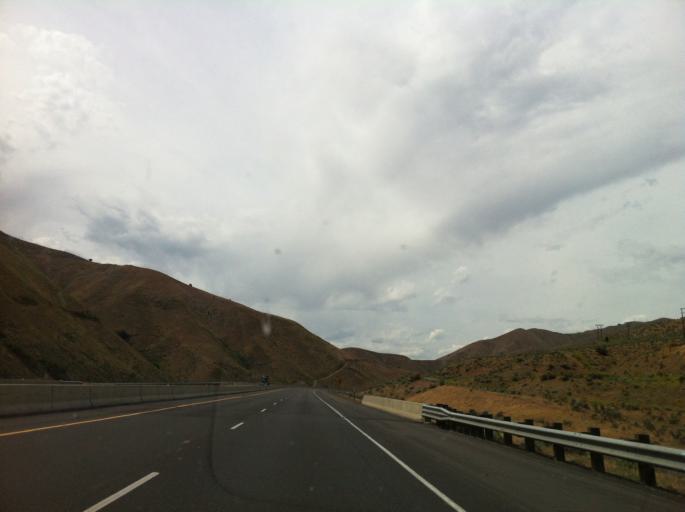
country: US
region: Idaho
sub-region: Washington County
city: Weiser
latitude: 44.4277
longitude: -117.3150
